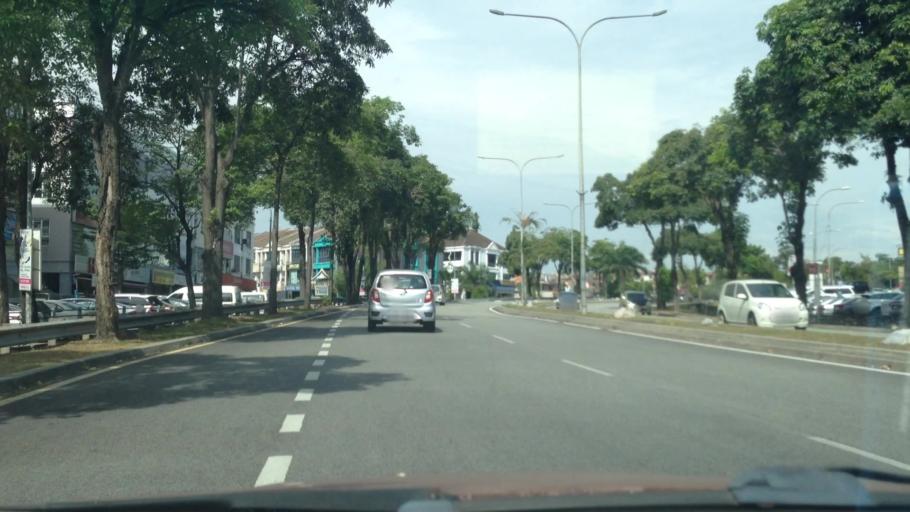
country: MY
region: Selangor
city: Subang Jaya
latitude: 3.0478
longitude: 101.5871
